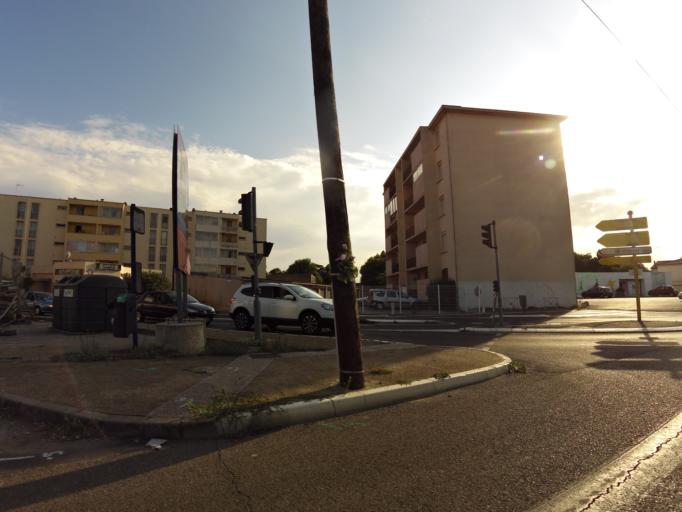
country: FR
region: Languedoc-Roussillon
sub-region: Departement de l'Herault
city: Lunel
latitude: 43.6763
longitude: 4.1258
